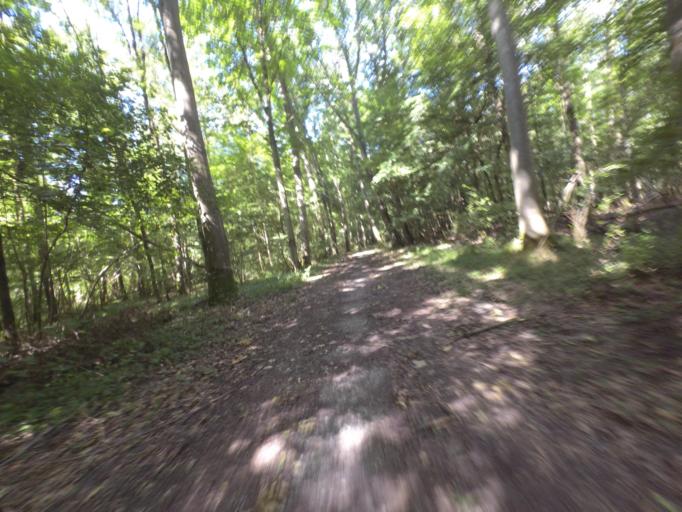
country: DE
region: Baden-Wuerttemberg
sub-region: Karlsruhe Region
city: Ottenhofen
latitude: 48.7543
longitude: 8.1275
